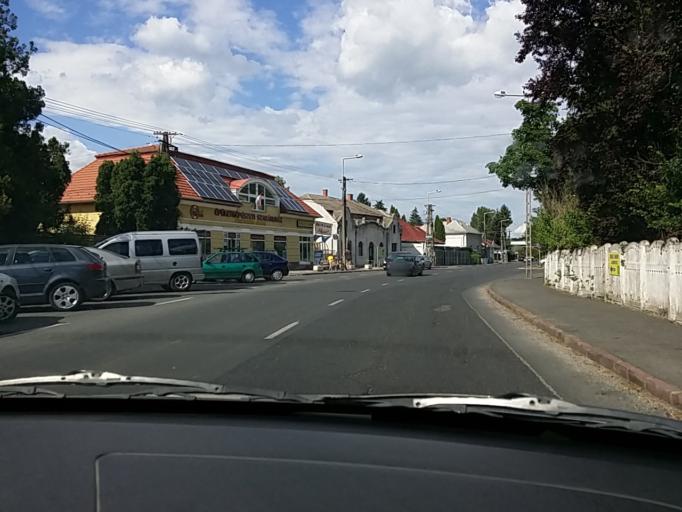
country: HU
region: Veszprem
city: Revfueloep
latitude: 46.8278
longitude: 17.6293
